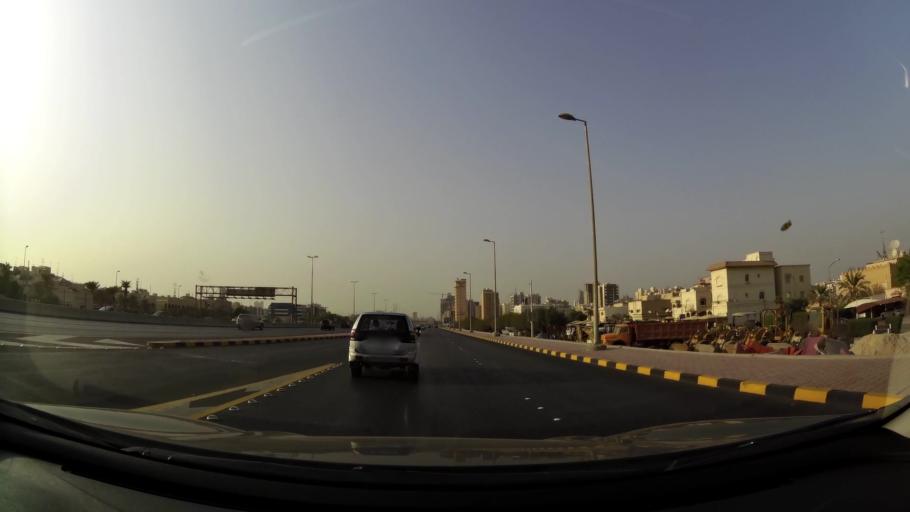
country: KW
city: Bayan
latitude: 29.3192
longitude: 48.0493
